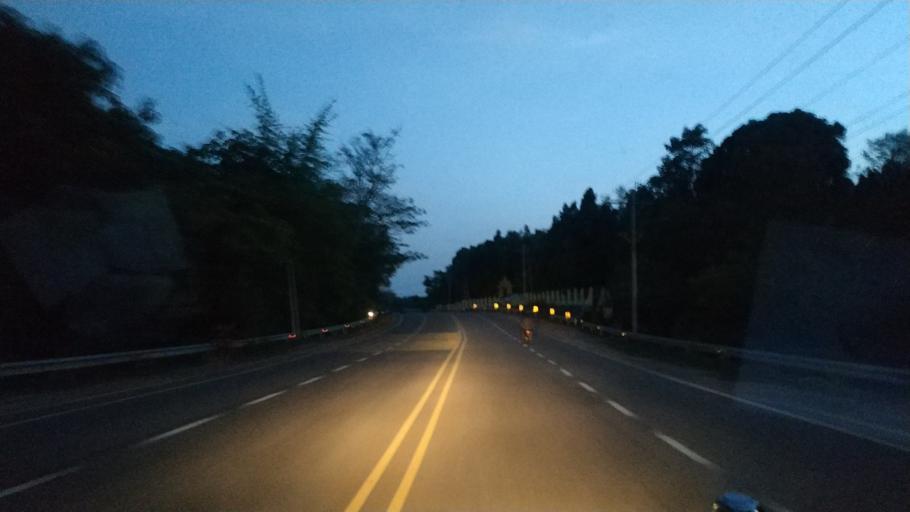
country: MM
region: Mon
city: Kyaikto
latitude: 17.3525
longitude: 97.0394
